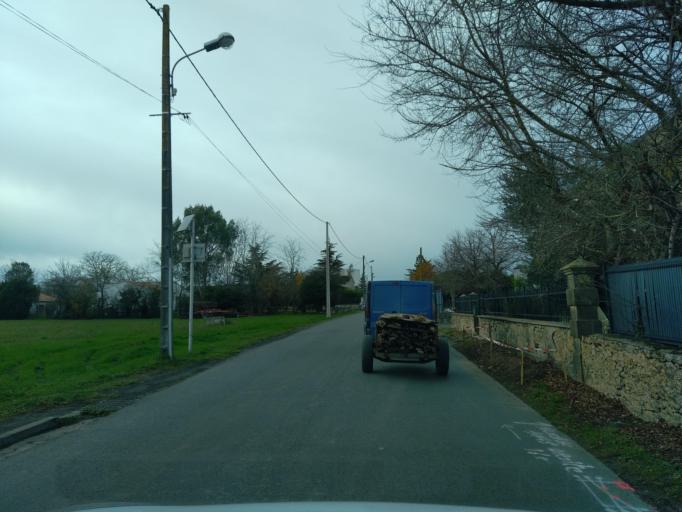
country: FR
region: Pays de la Loire
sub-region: Departement de la Vendee
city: Vix
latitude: 46.3670
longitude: -0.8647
